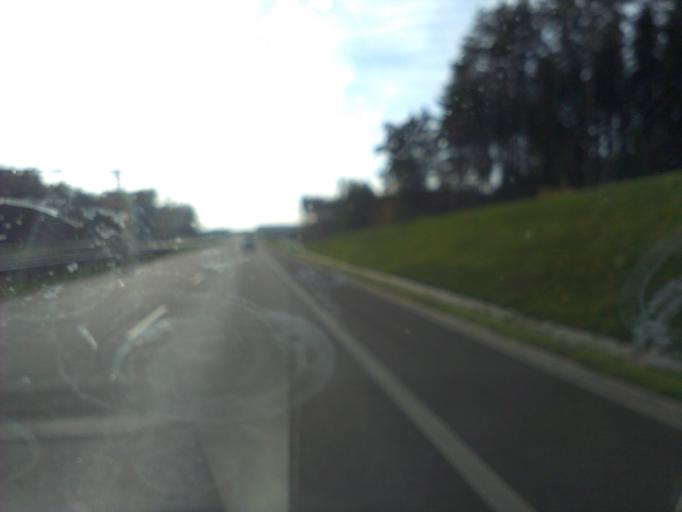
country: PL
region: West Pomeranian Voivodeship
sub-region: Powiat mysliborski
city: Mysliborz
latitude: 53.0164
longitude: 14.8616
